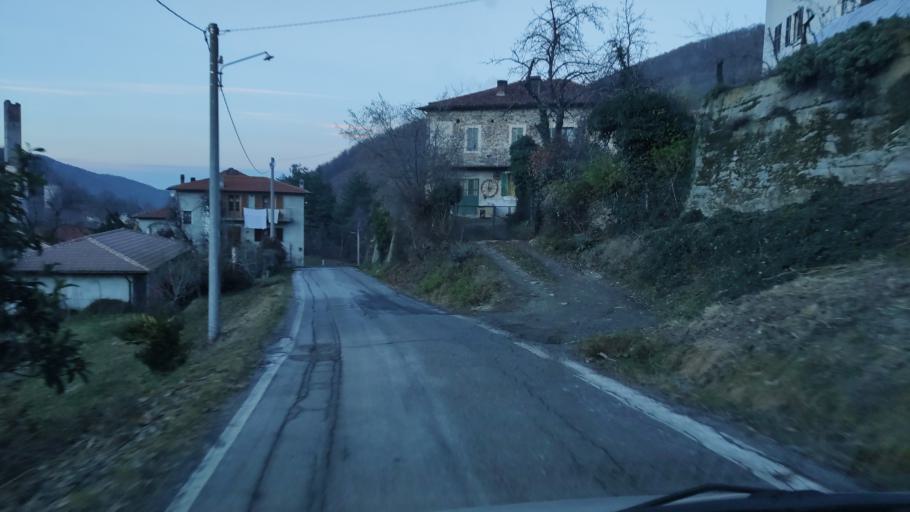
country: IT
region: Piedmont
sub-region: Provincia di Cuneo
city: Lisio
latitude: 44.2917
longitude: 7.9828
